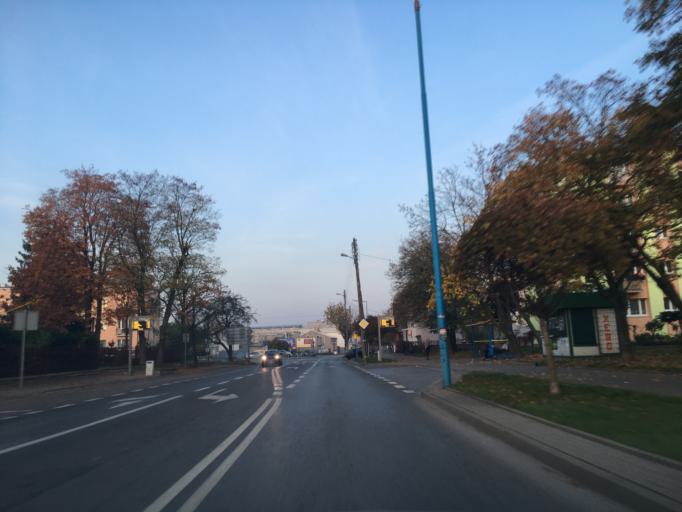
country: PL
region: Lodz Voivodeship
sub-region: Skierniewice
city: Skierniewice
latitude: 51.9559
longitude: 20.1514
